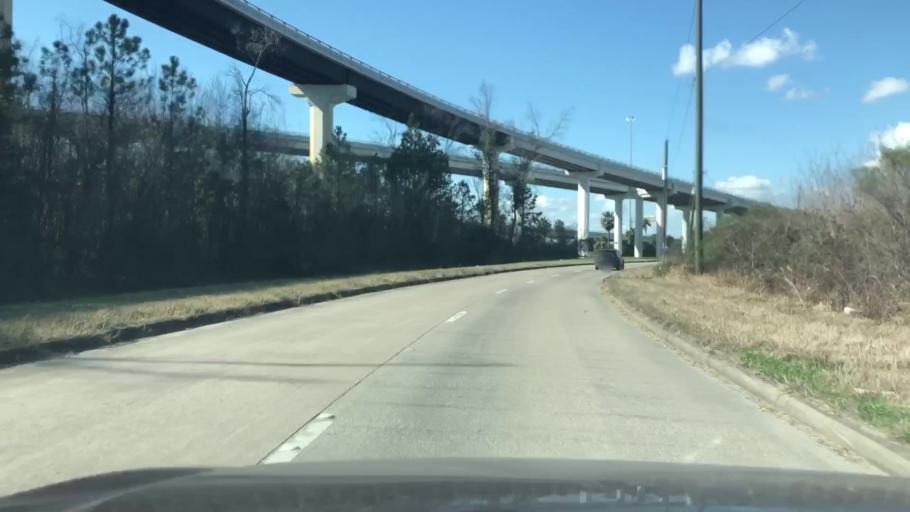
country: US
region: Texas
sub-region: Harris County
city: South Houston
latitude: 29.6086
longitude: -95.2053
